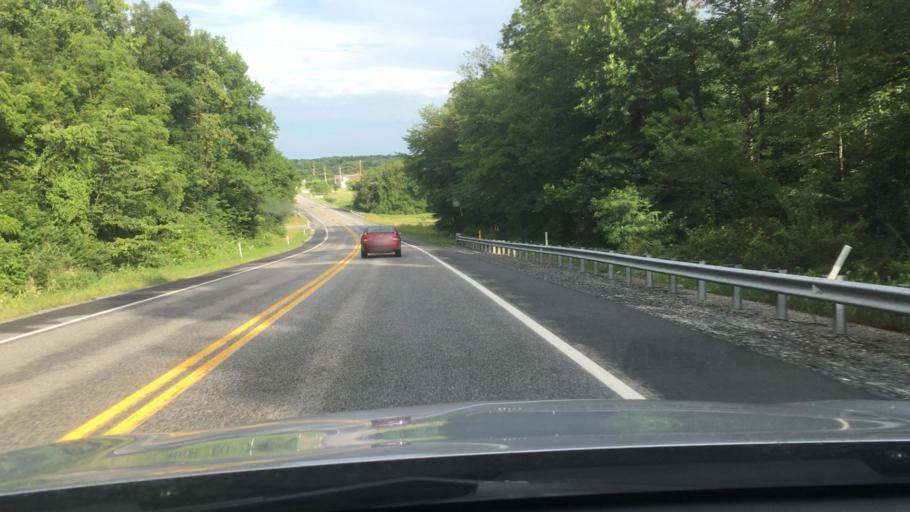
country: US
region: Pennsylvania
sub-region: York County
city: Dillsburg
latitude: 40.0823
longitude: -76.9387
